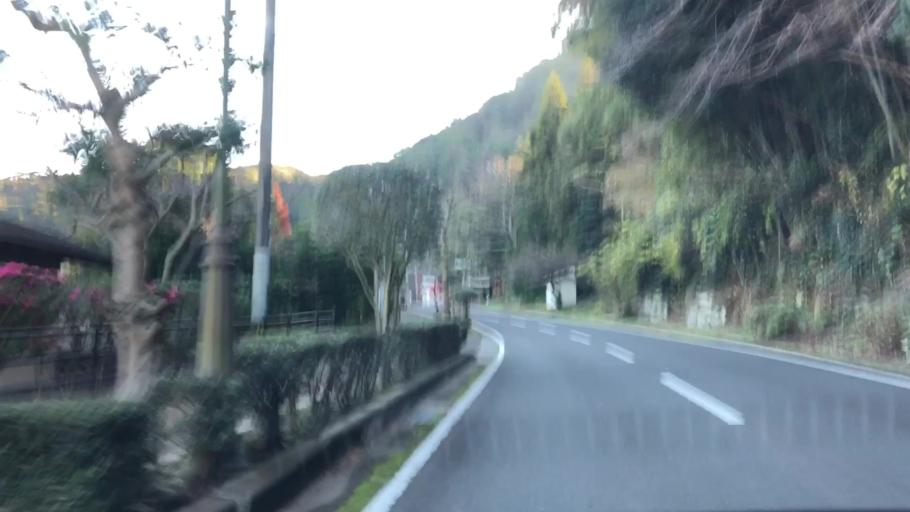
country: JP
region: Nagasaki
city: Sasebo
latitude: 33.0240
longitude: 129.6592
